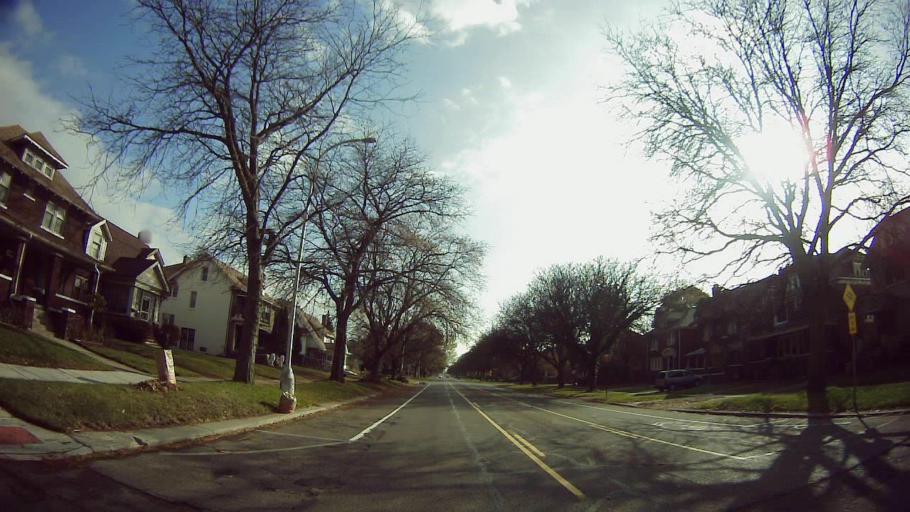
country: US
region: Michigan
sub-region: Wayne County
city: Highland Park
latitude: 42.3627
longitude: -83.1125
